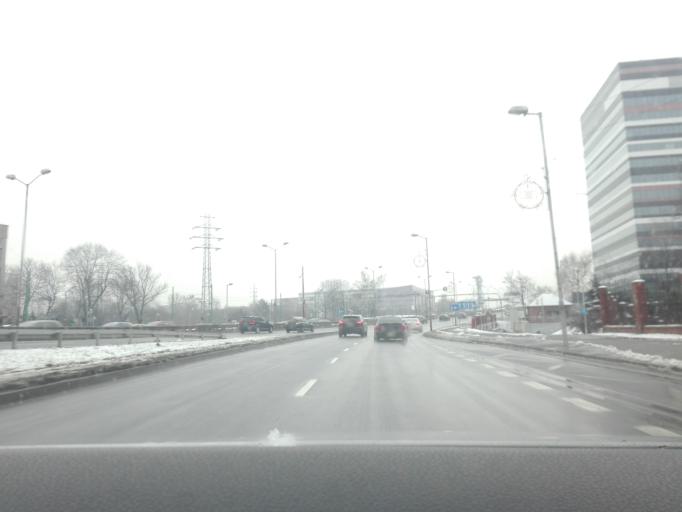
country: PL
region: Silesian Voivodeship
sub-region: Katowice
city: Katowice
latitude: 50.2708
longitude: 18.9954
